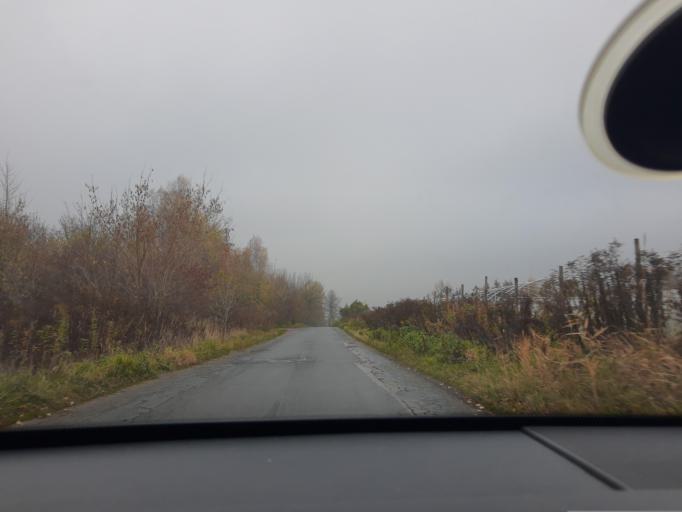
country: PL
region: Lodz Voivodeship
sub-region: Powiat pabianicki
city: Konstantynow Lodzki
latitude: 51.7481
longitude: 19.3718
